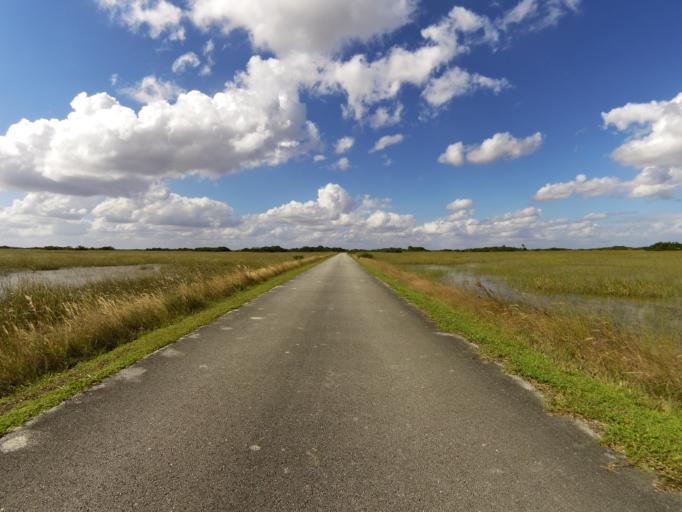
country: US
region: Florida
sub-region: Miami-Dade County
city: The Hammocks
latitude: 25.6942
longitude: -80.7601
